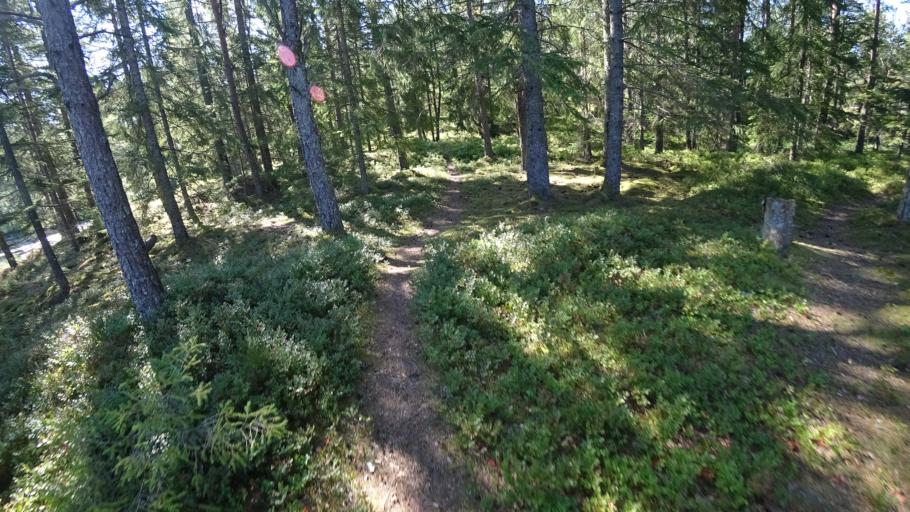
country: SE
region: Vaestra Goetaland
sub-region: Munkedals Kommun
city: Munkedal
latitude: 58.7216
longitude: 11.7332
